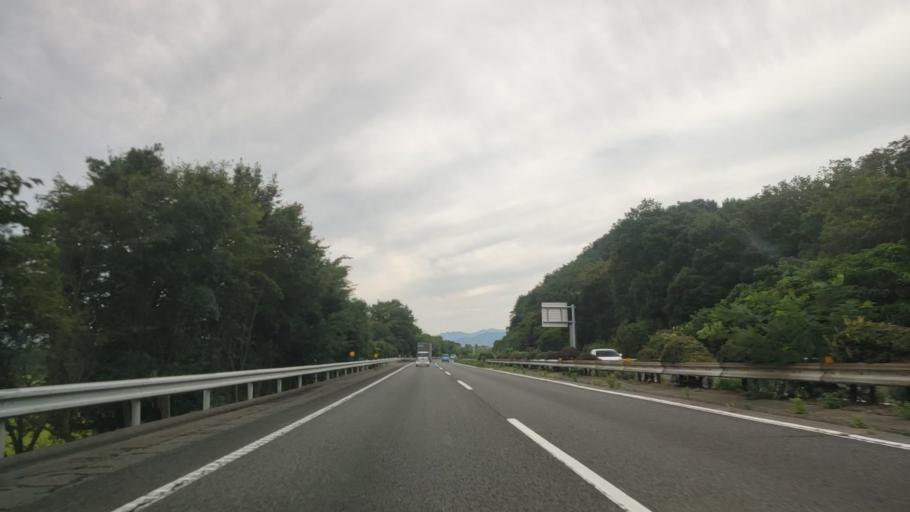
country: JP
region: Shiga Prefecture
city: Youkaichi
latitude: 35.0677
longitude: 136.1546
